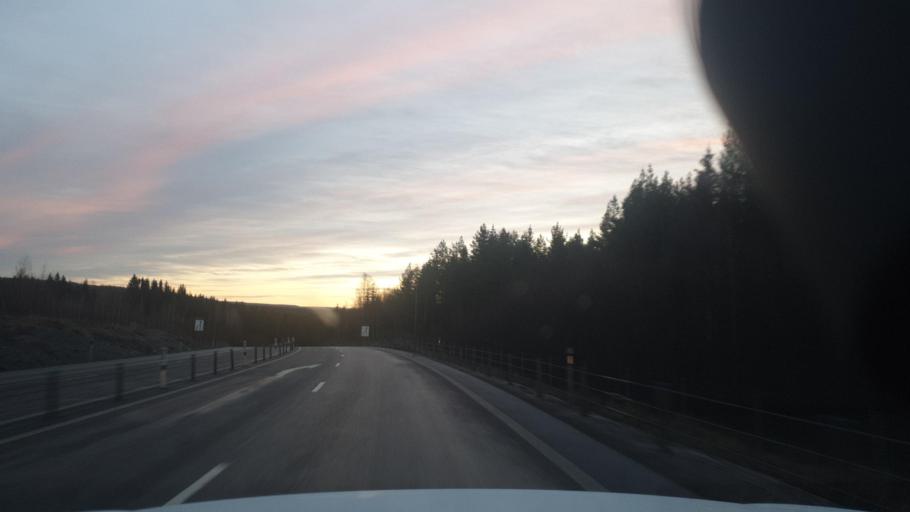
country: SE
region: Vaermland
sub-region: Eda Kommun
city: Amotfors
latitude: 59.7592
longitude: 12.4622
